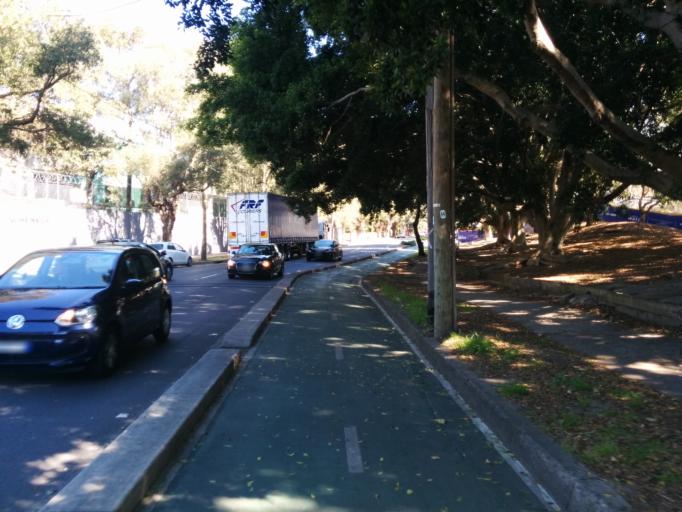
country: AU
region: New South Wales
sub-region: City of Sydney
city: Alexandria
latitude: -33.9084
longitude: 151.1972
